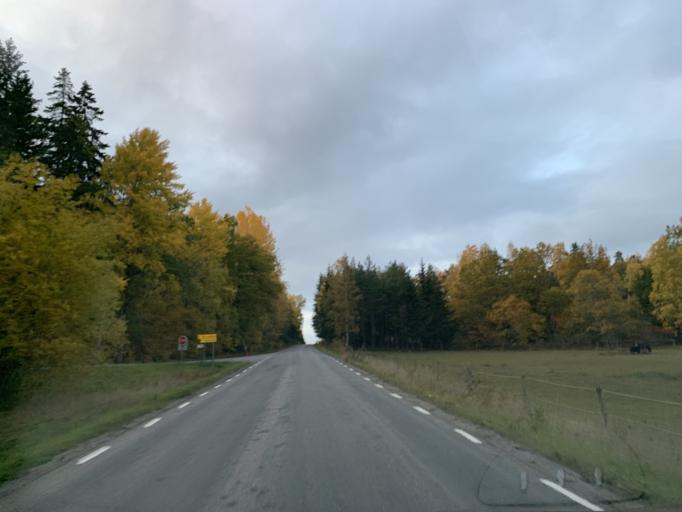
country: SE
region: Stockholm
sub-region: Nynashamns Kommun
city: Osmo
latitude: 58.9338
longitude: 17.7635
